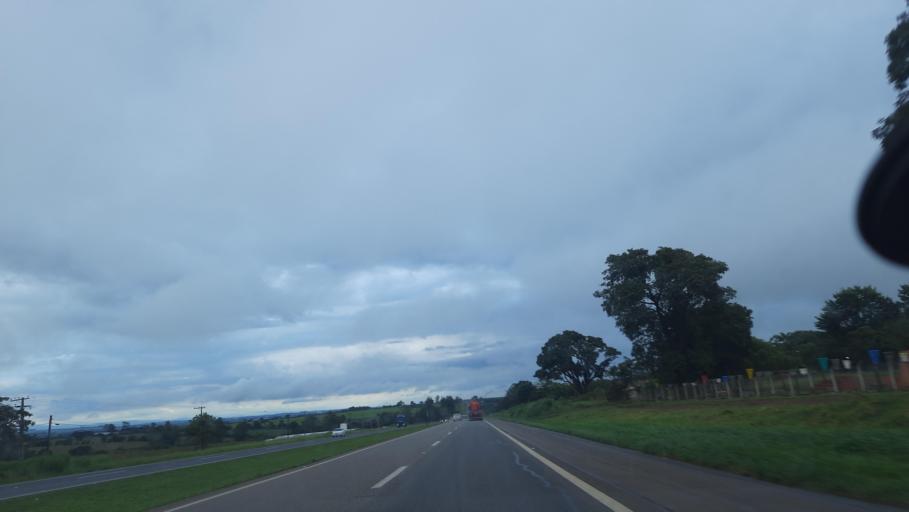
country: BR
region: Sao Paulo
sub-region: Moji-Guacu
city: Mogi-Gaucu
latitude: -22.2310
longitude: -46.9788
